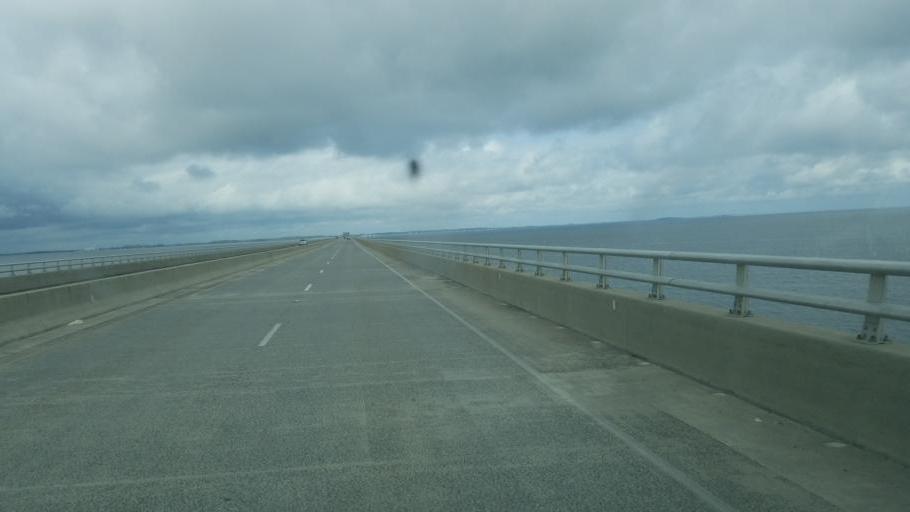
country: US
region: North Carolina
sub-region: Dare County
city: Manteo
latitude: 35.8824
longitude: -75.6867
